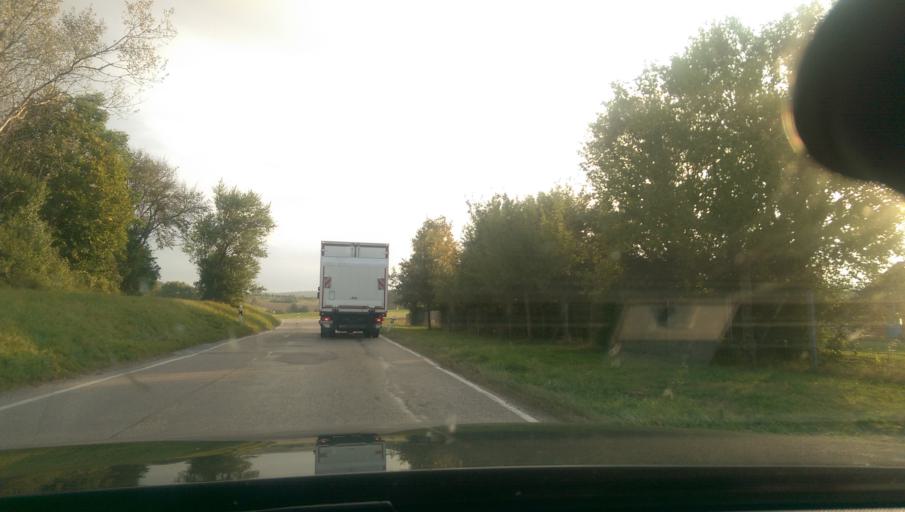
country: DE
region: Baden-Wuerttemberg
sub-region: Karlsruhe Region
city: Friolzheim
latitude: 48.8248
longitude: 8.8342
